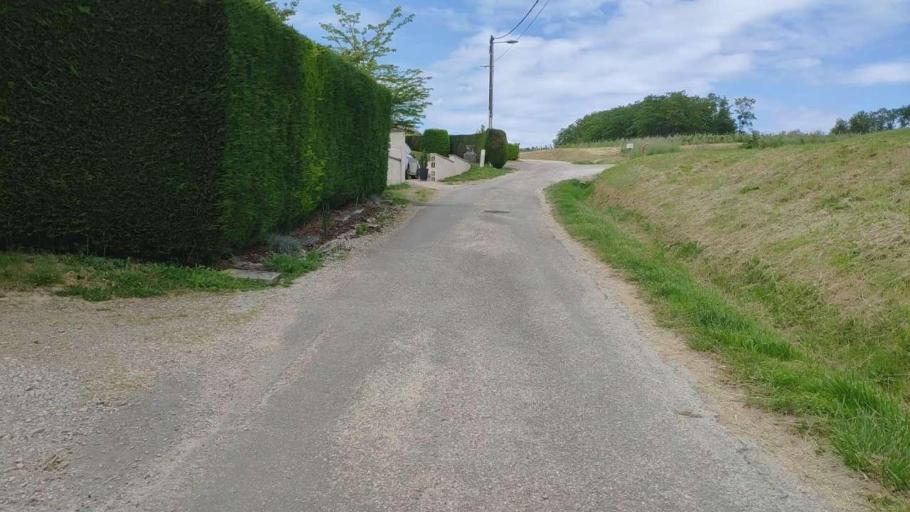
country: FR
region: Franche-Comte
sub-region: Departement du Jura
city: Montmorot
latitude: 46.7354
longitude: 5.5184
